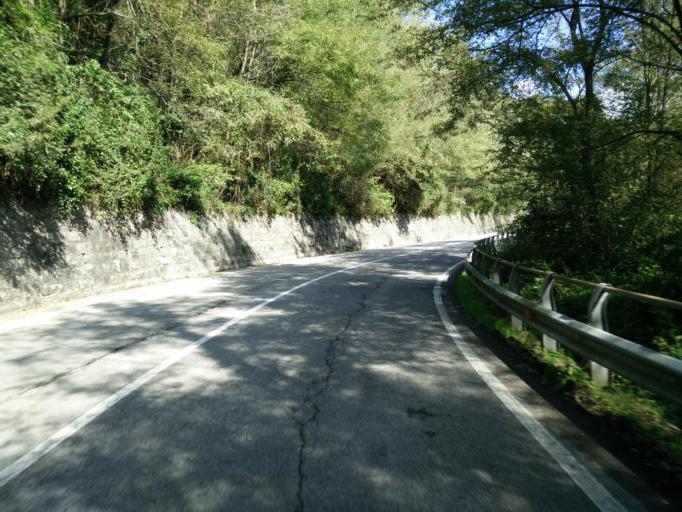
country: IT
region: Liguria
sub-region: Provincia di La Spezia
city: Carrodano
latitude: 44.2454
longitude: 9.6816
